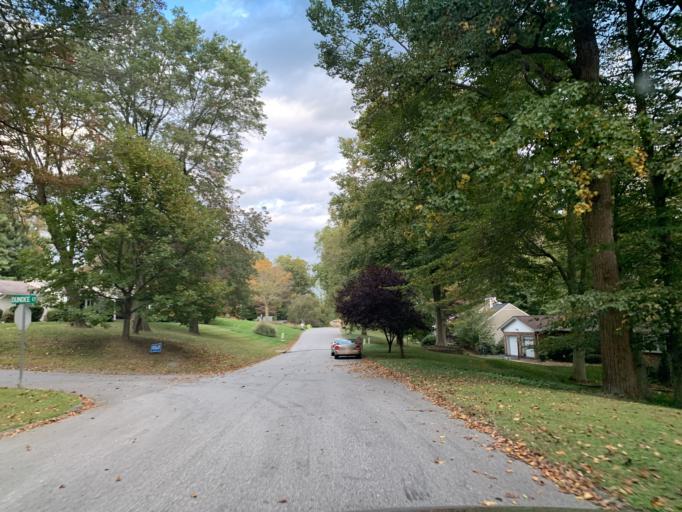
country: US
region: Maryland
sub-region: Harford County
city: Bel Air South
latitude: 39.5149
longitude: -76.3213
